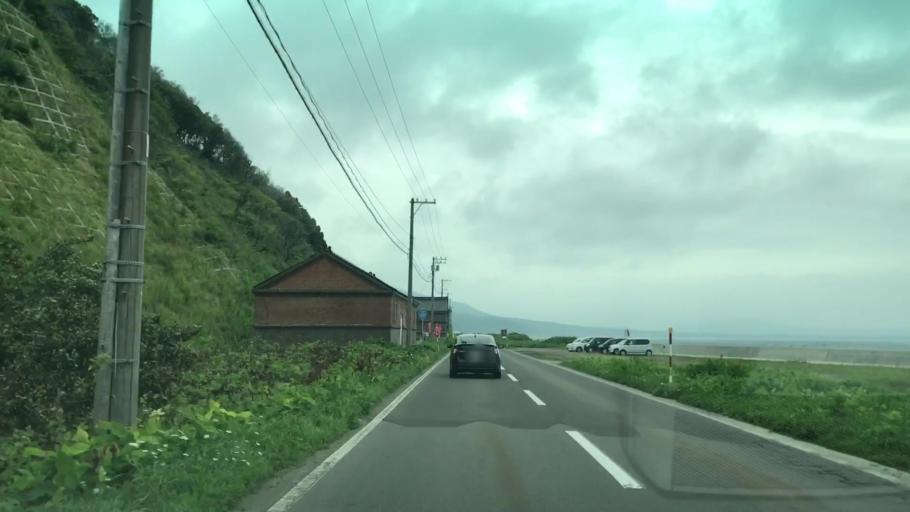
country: JP
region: Hokkaido
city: Iwanai
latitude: 42.8105
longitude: 140.3043
